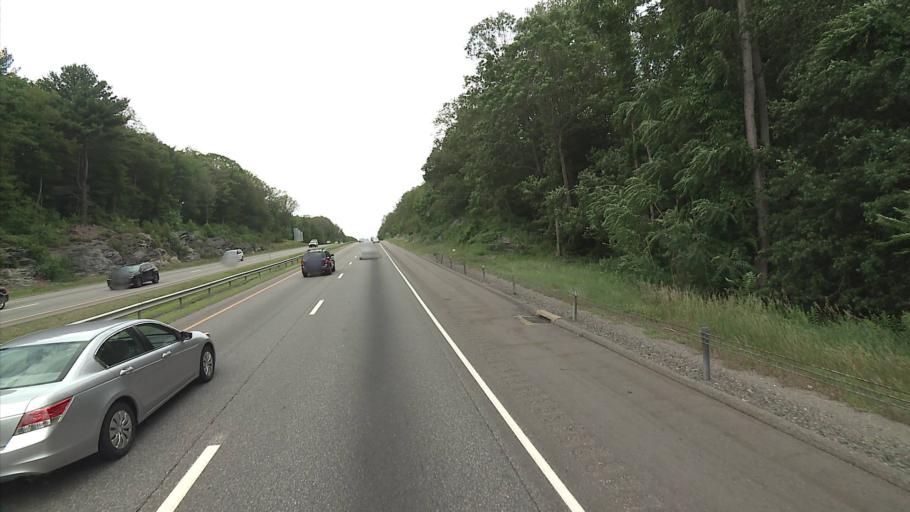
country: US
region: Connecticut
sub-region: New London County
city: Norwich
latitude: 41.5264
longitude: -72.1170
